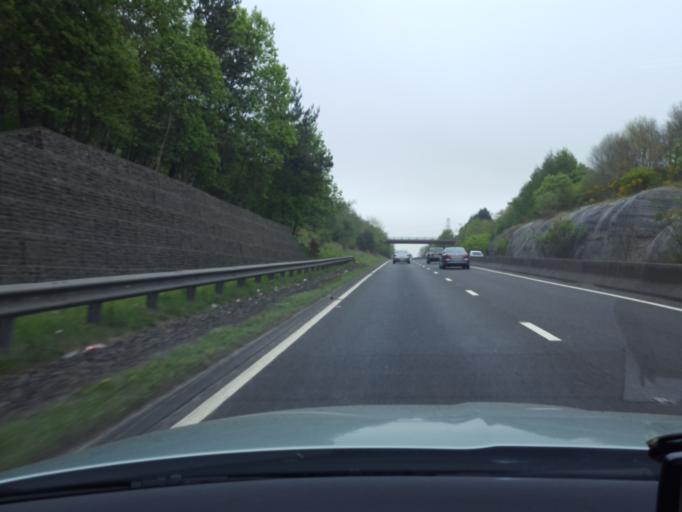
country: GB
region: Scotland
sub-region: Dundee City
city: Dundee
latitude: 56.5015
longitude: -2.9486
